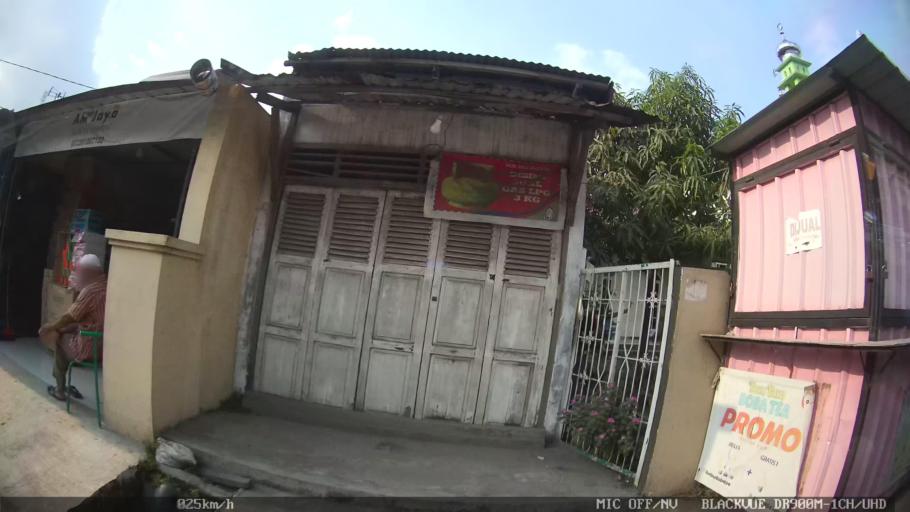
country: ID
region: North Sumatra
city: Medan
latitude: 3.5854
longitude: 98.7413
